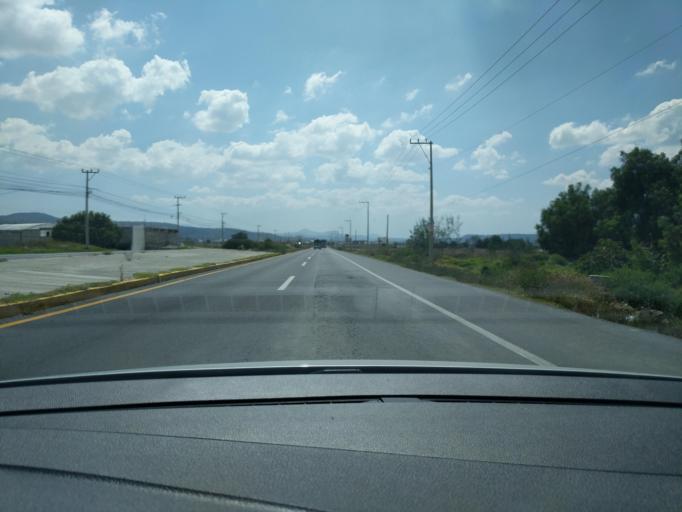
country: MX
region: Hidalgo
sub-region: Mineral de la Reforma
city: Rinconada de los Angeles
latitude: 20.0290
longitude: -98.7270
